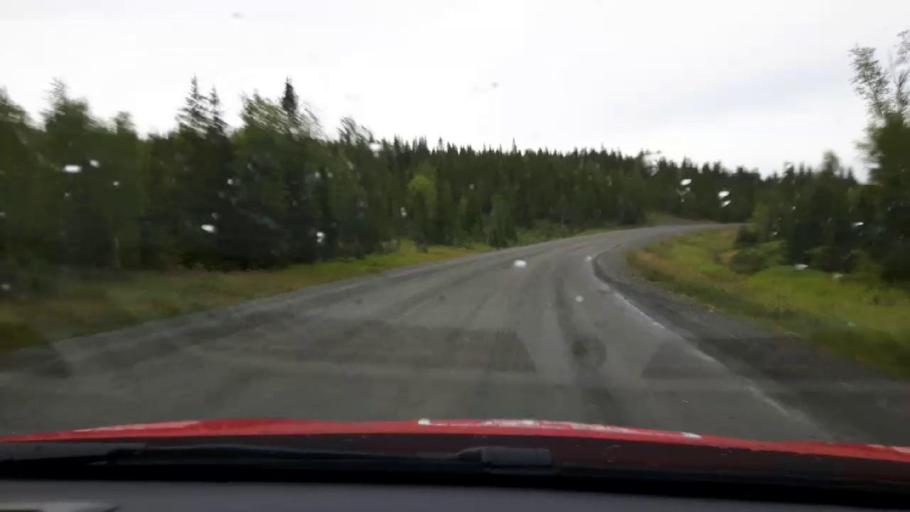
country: SE
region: Jaemtland
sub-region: Are Kommun
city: Are
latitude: 63.4151
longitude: 12.7643
